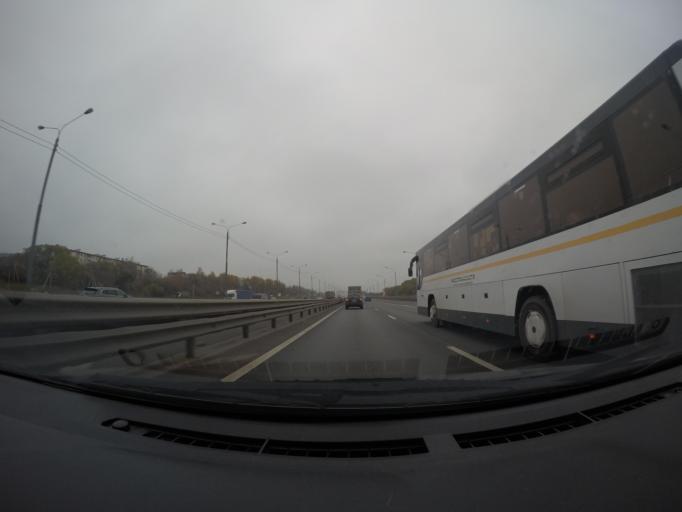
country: RU
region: Moskovskaya
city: Shcherbinka
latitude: 55.4707
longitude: 37.6176
